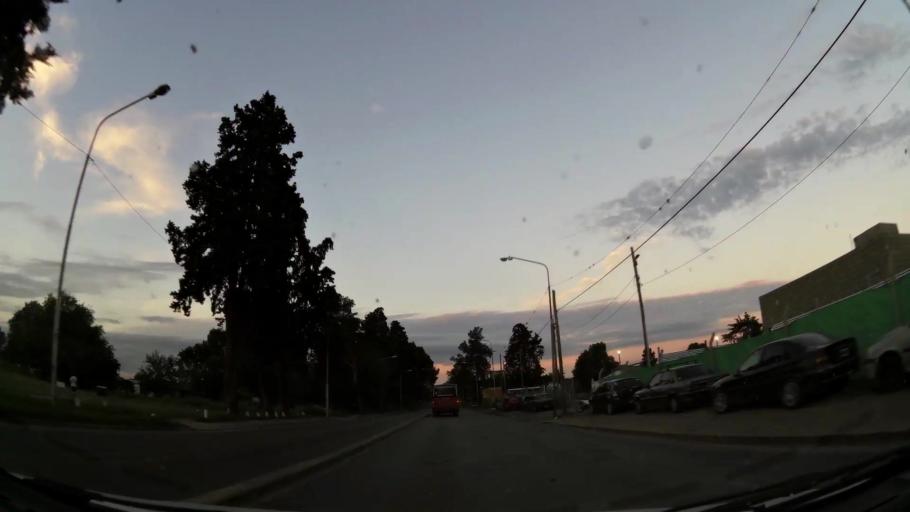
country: AR
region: Buenos Aires
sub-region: Partido de Merlo
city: Merlo
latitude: -34.6833
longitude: -58.7614
